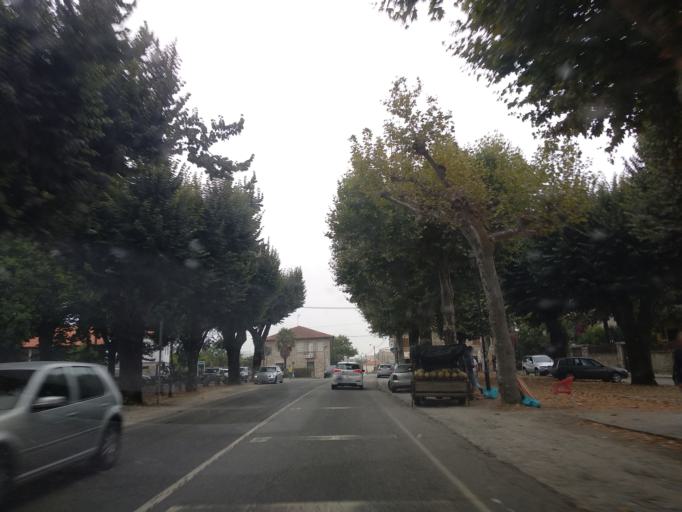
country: PT
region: Braga
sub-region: Vila Verde
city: Vila Verde
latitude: 41.6268
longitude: -8.4333
